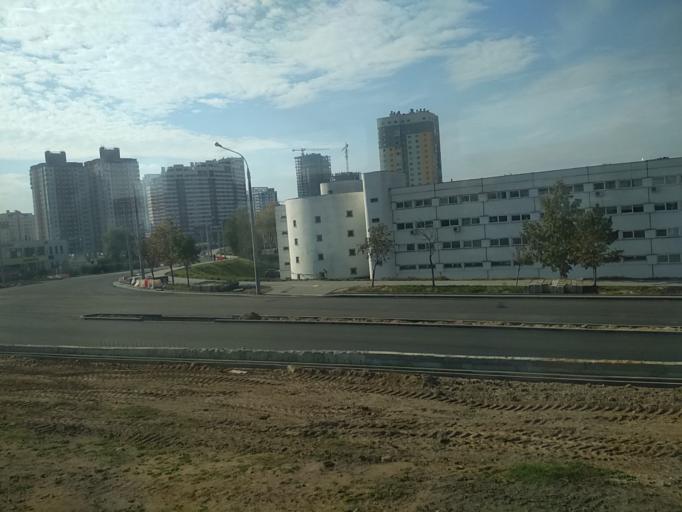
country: BY
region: Minsk
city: Minsk
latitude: 53.8738
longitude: 27.5621
